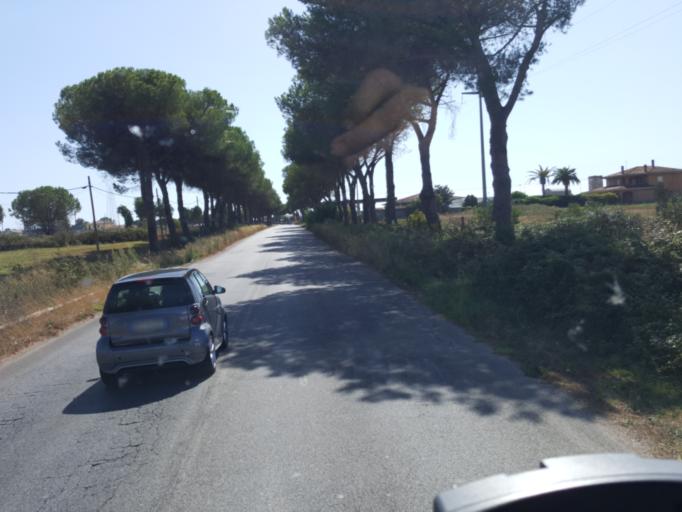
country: IT
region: Latium
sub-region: Provincia di Latina
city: Genio Civile
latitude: 41.5250
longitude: 12.7042
